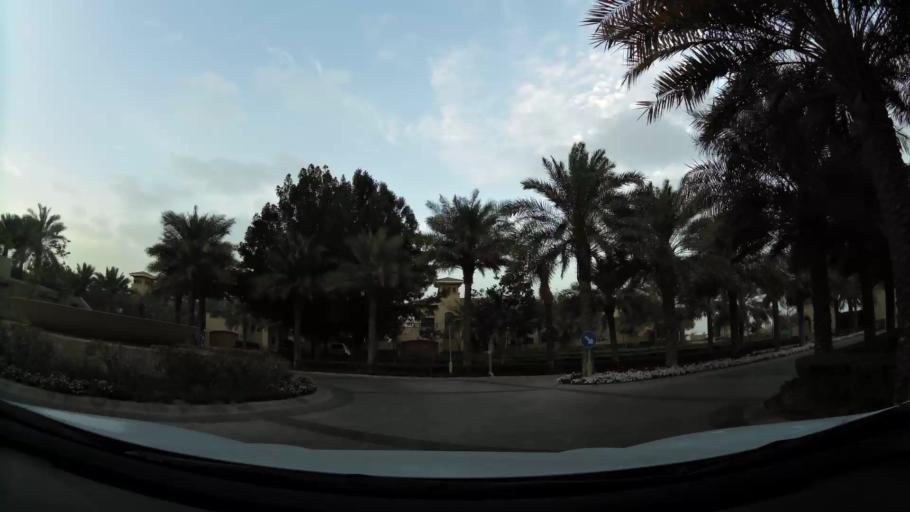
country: AE
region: Abu Dhabi
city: Abu Dhabi
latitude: 24.5372
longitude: 54.4270
